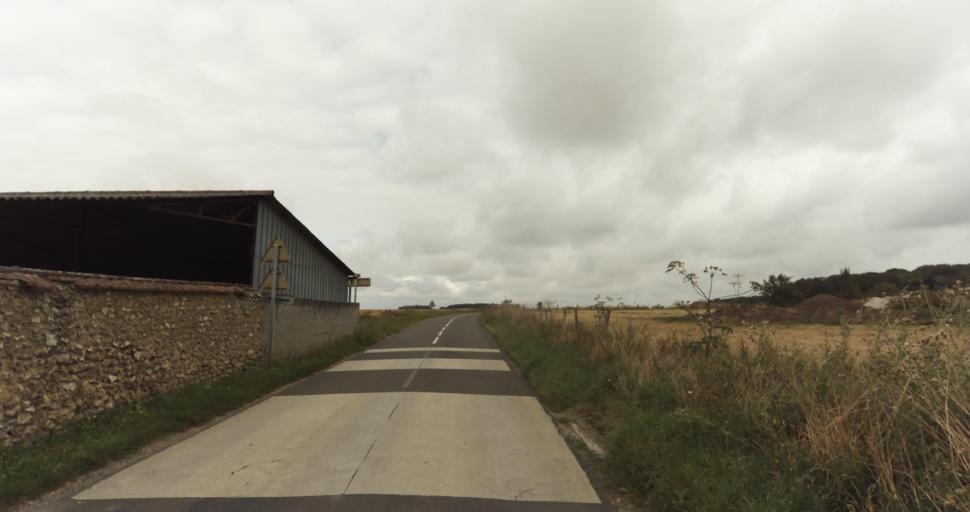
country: FR
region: Haute-Normandie
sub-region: Departement de l'Eure
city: Pacy-sur-Eure
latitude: 48.9519
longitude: 1.3518
